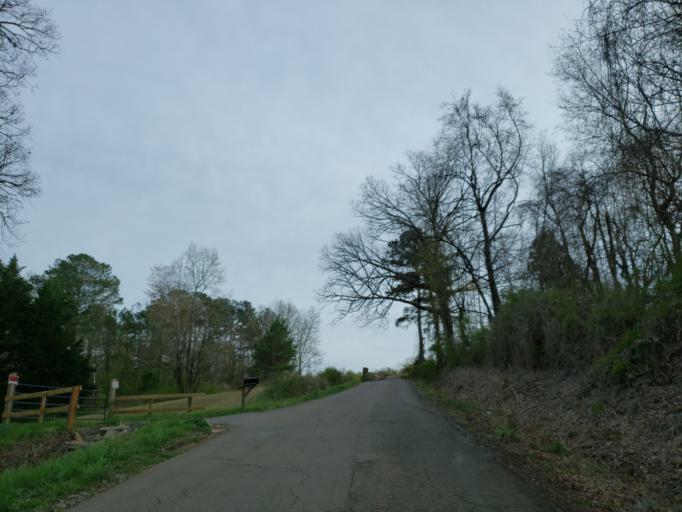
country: US
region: Georgia
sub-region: Pickens County
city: Nelson
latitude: 34.3894
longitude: -84.4343
